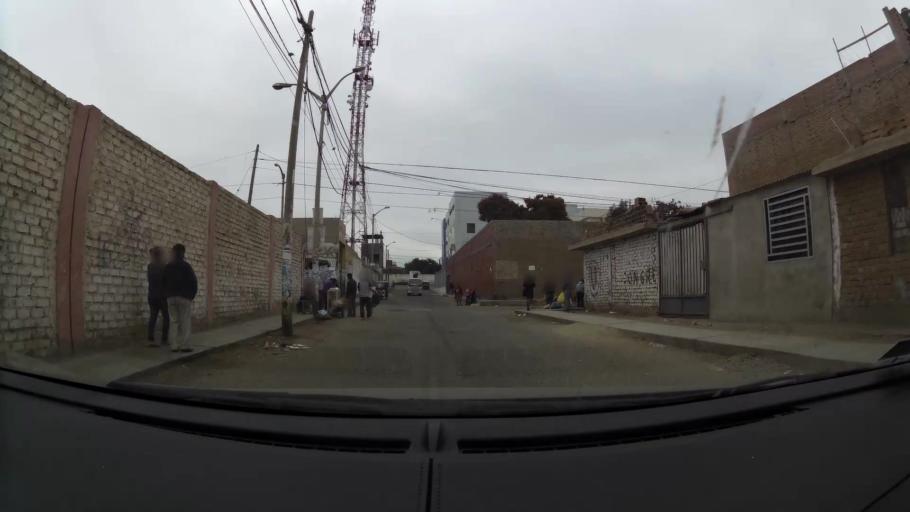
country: PE
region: La Libertad
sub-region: Provincia de Trujillo
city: La Esperanza
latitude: -8.0799
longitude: -79.0470
